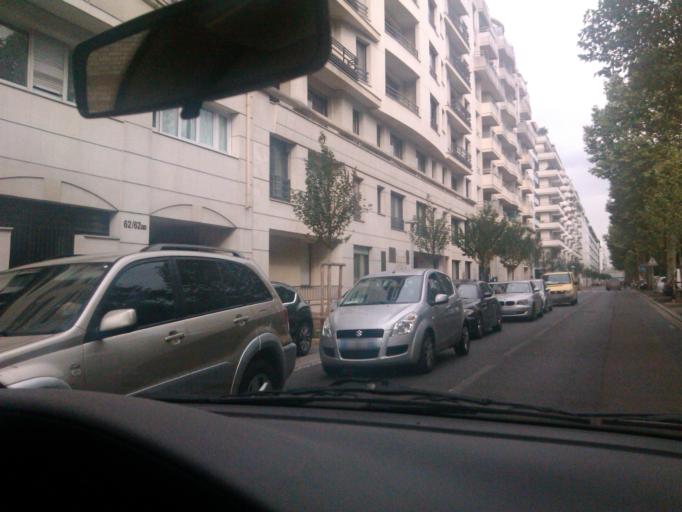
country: FR
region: Ile-de-France
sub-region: Departement des Hauts-de-Seine
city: Issy-les-Moulineaux
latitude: 48.8280
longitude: 2.2675
